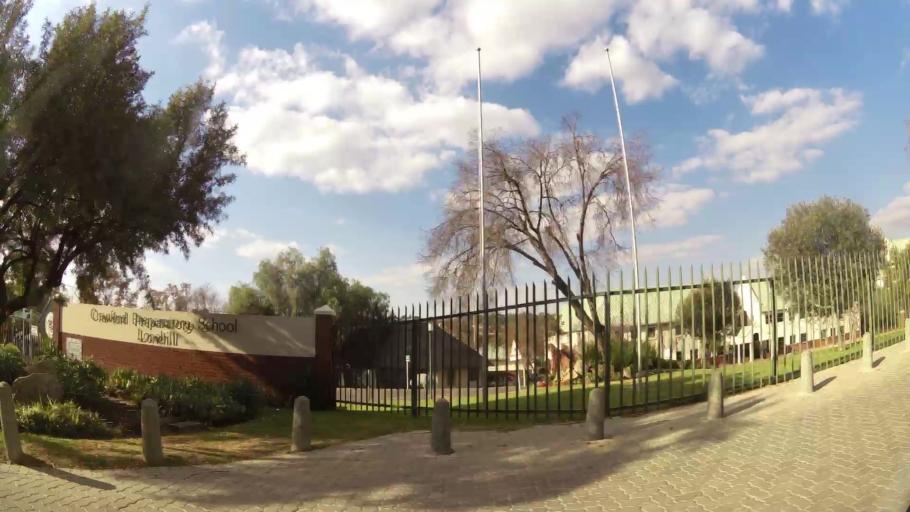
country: ZA
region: Gauteng
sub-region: City of Johannesburg Metropolitan Municipality
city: Diepsloot
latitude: -26.0085
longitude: 28.0325
